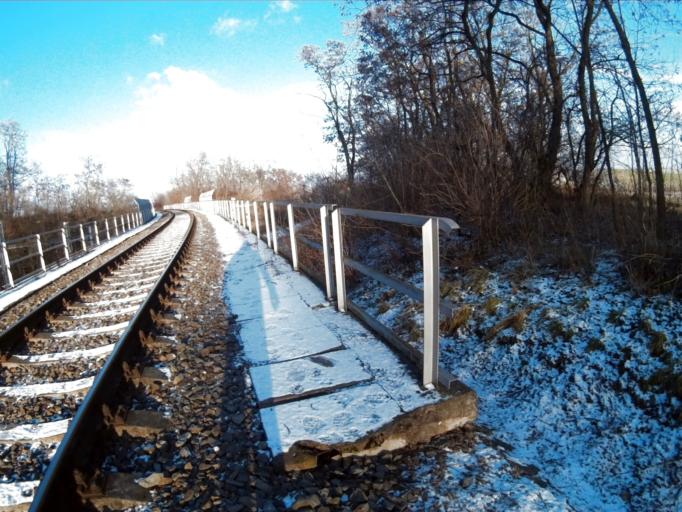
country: CZ
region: South Moravian
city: Blazovice
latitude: 49.1662
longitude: 16.8101
